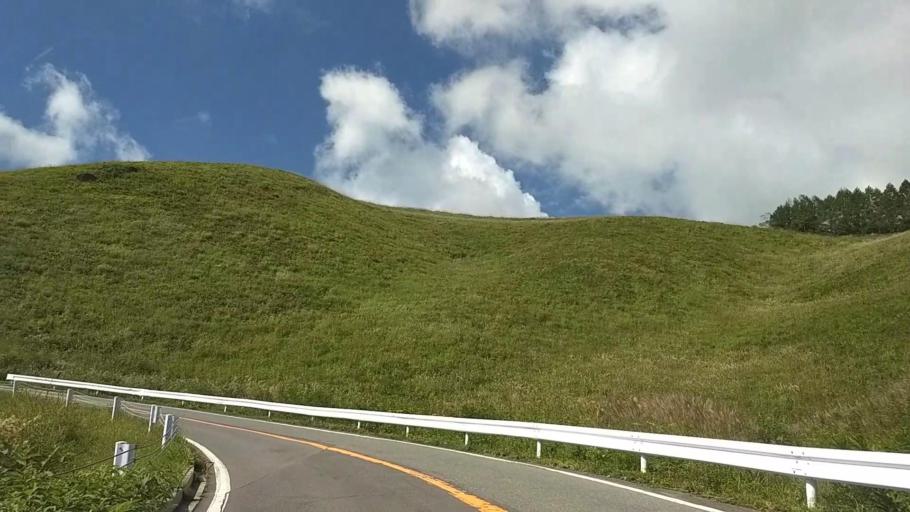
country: JP
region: Nagano
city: Suwa
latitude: 36.1016
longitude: 138.2183
